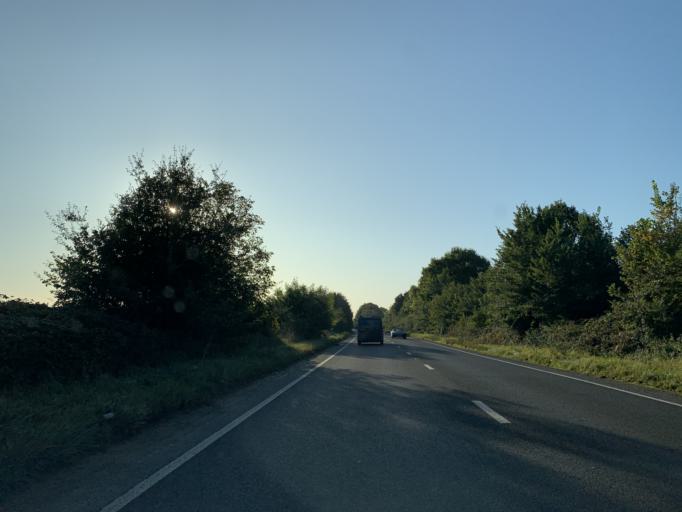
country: GB
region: England
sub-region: Wiltshire
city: Whiteparish
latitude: 51.0084
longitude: -1.6741
